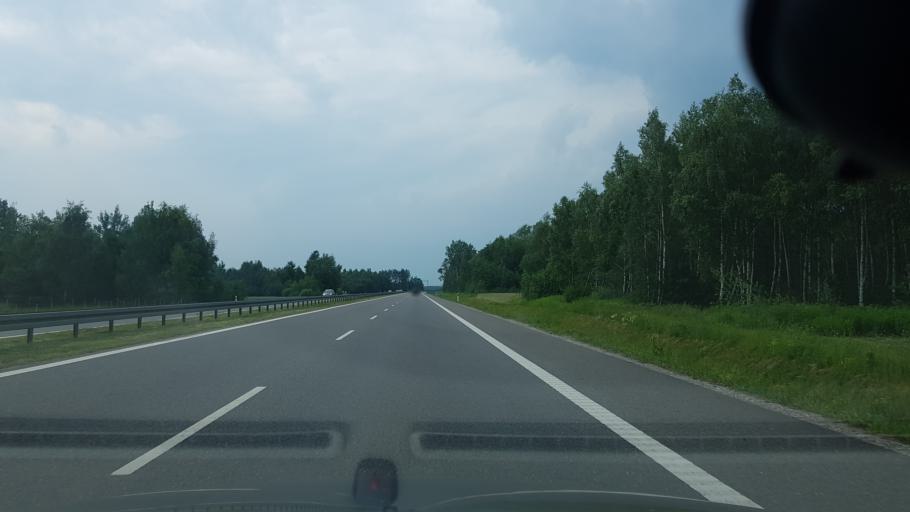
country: PL
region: Masovian Voivodeship
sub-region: Powiat legionowski
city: Serock
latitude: 52.4975
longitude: 21.0478
